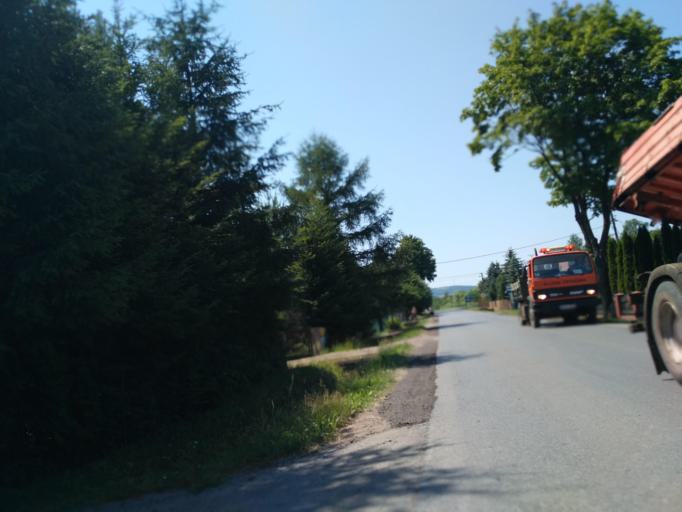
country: PL
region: Subcarpathian Voivodeship
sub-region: Powiat sanocki
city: Niebieszczany
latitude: 49.5395
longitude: 22.1310
